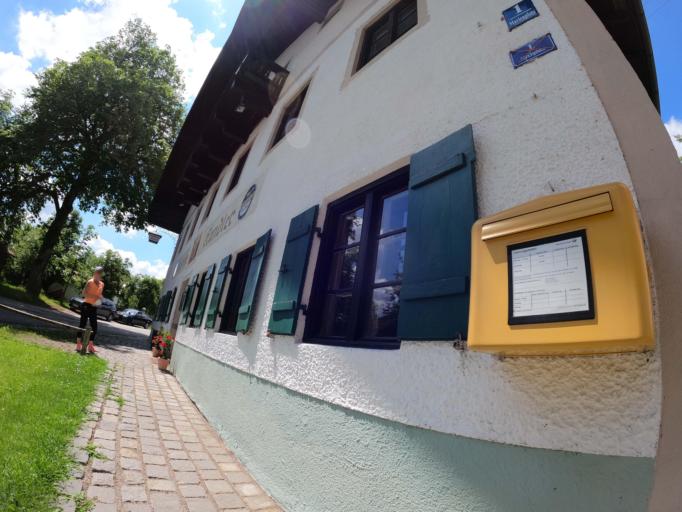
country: DE
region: Bavaria
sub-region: Upper Bavaria
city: Oberhaching
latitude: 47.9807
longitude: 11.5713
